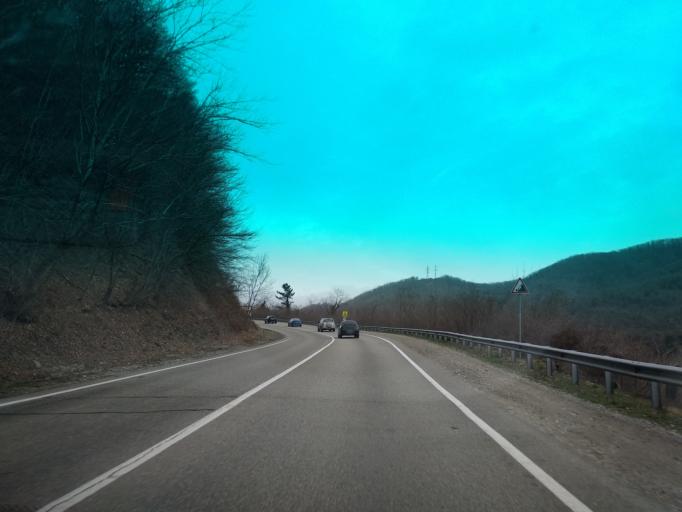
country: RU
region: Krasnodarskiy
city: Ol'ginka
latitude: 44.2206
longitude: 38.8947
